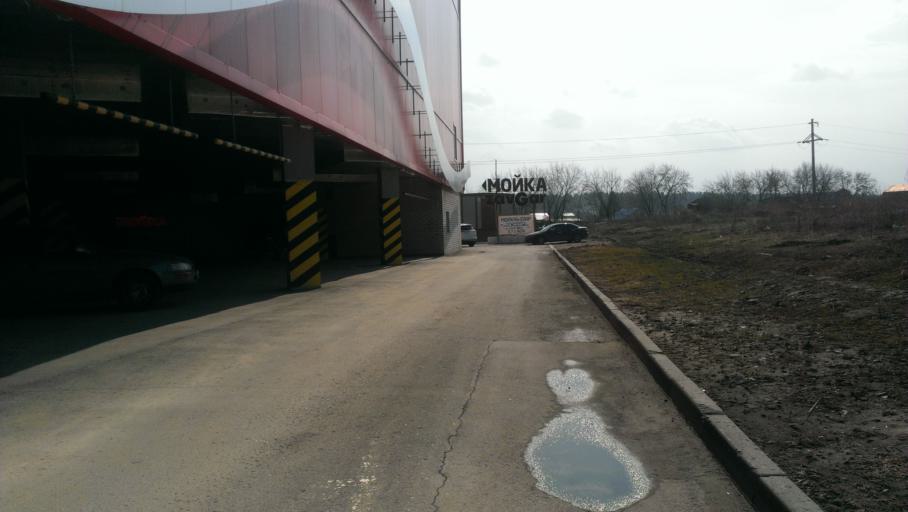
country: RU
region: Altai Krai
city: Novosilikatnyy
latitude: 53.3259
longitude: 83.6894
